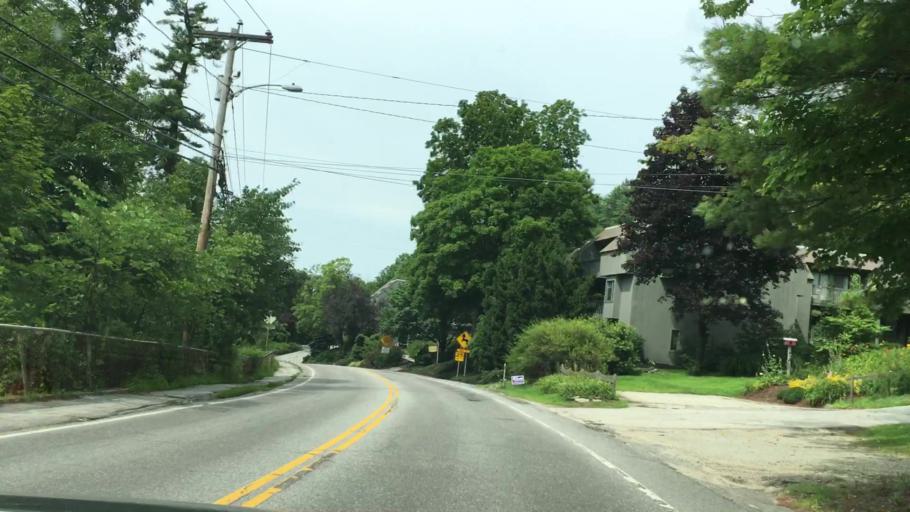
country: US
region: New Hampshire
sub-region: Hillsborough County
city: Peterborough
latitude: 42.8761
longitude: -71.9479
